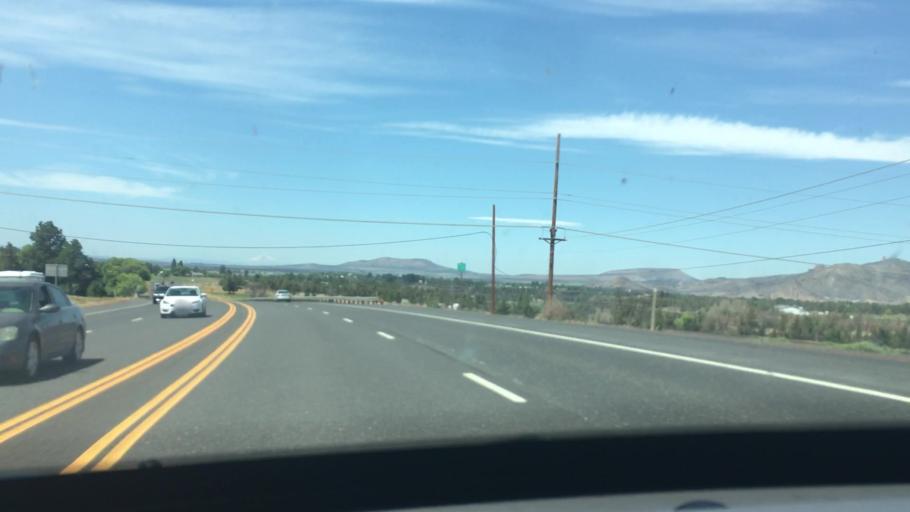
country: US
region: Oregon
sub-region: Deschutes County
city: Terrebonne
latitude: 44.3181
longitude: -121.1712
